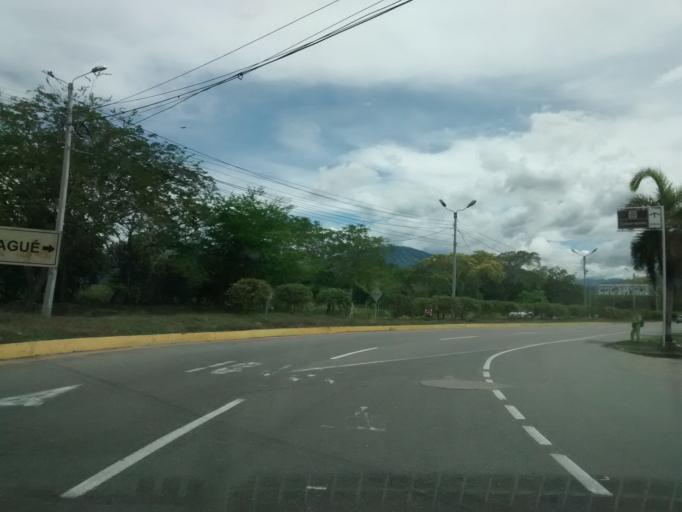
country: CO
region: Tolima
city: Ibague
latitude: 4.4003
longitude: -75.1460
